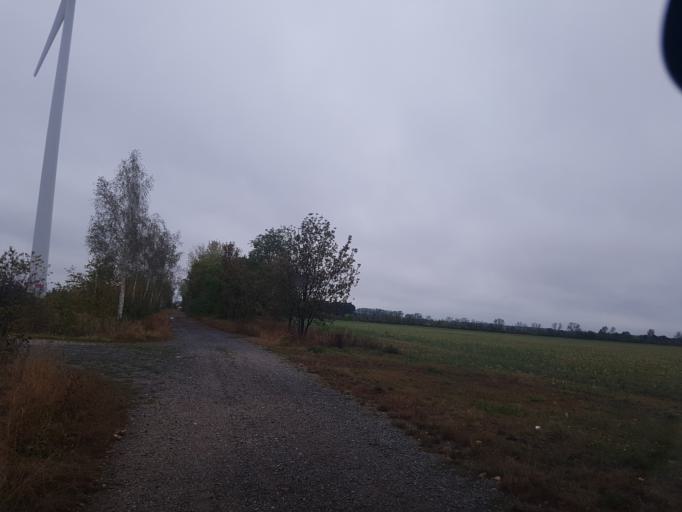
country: DE
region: Brandenburg
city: Merzdorf
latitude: 51.4218
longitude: 13.5077
